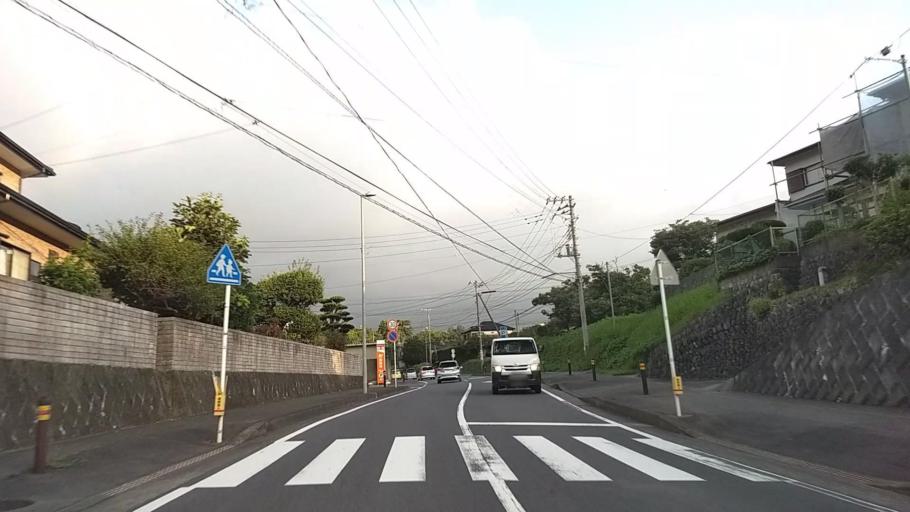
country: JP
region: Kanagawa
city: Atsugi
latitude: 35.4762
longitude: 139.2834
